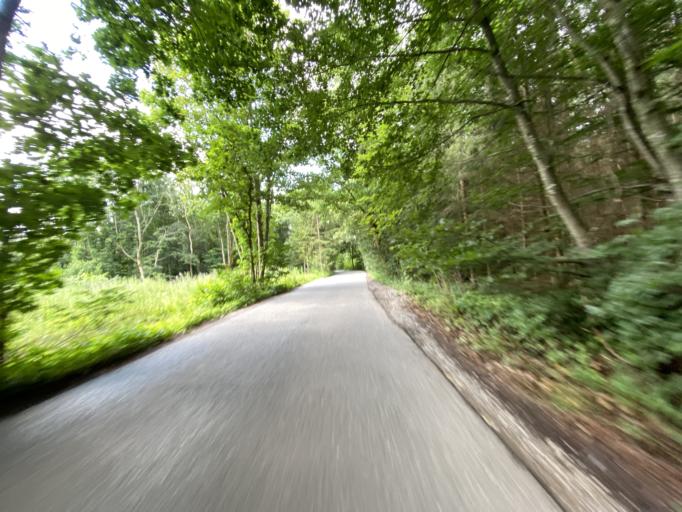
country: DE
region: Bavaria
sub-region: Upper Bavaria
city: Gilching
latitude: 48.0989
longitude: 11.3040
